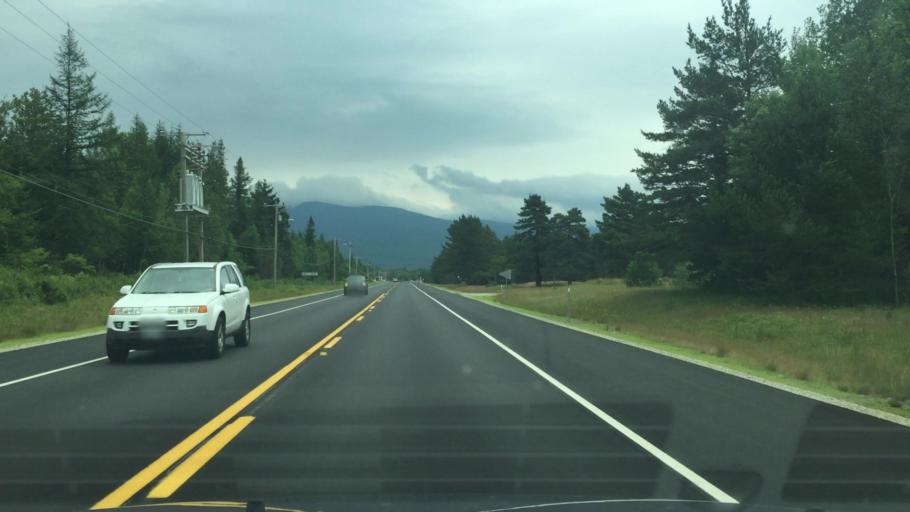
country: US
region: New Hampshire
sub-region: Coos County
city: Jefferson
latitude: 44.2682
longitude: -71.4679
